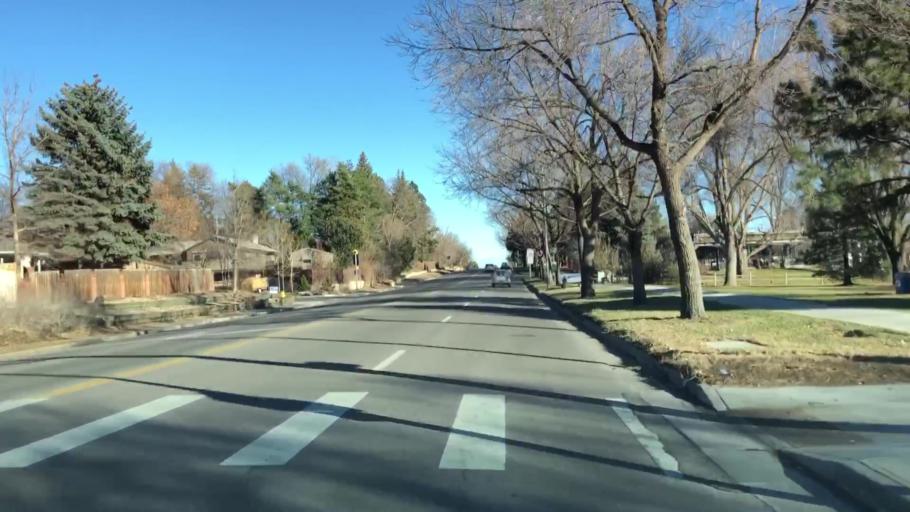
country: US
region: Colorado
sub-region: Larimer County
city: Fort Collins
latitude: 40.5666
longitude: -105.0524
